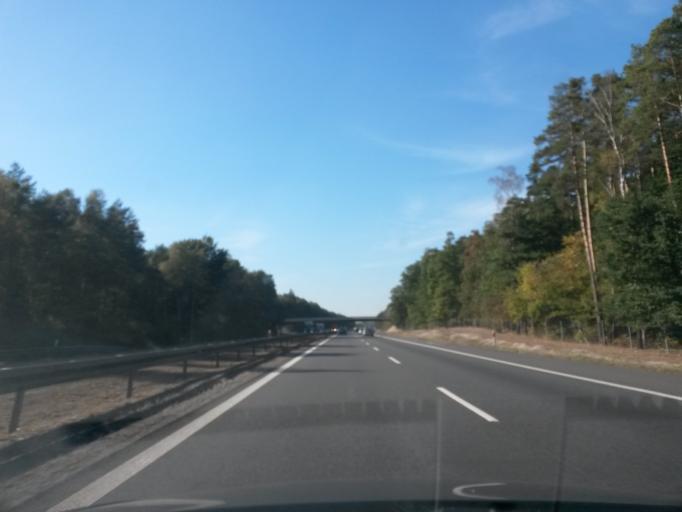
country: PL
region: Opole Voivodeship
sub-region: Powiat opolski
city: Proszkow
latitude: 50.5827
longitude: 17.8280
